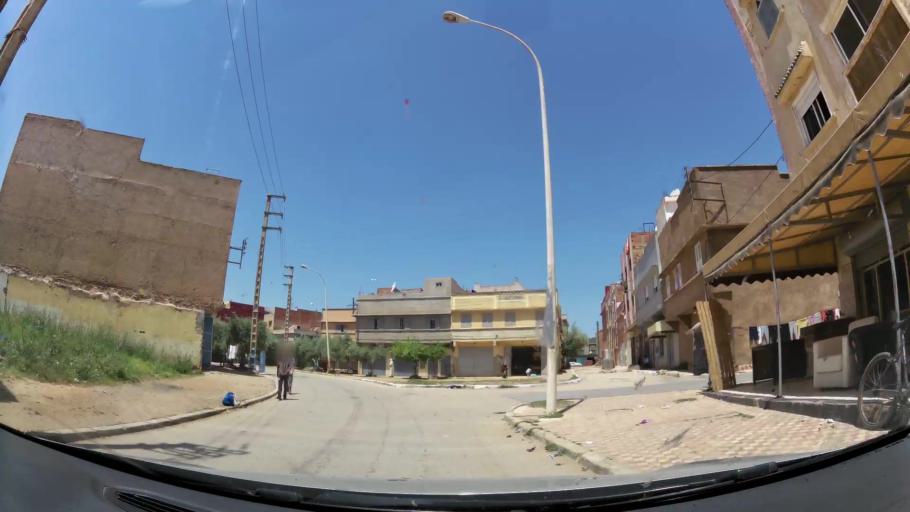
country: MA
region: Rabat-Sale-Zemmour-Zaer
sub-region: Khemisset
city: Khemisset
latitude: 33.8334
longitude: -6.0743
